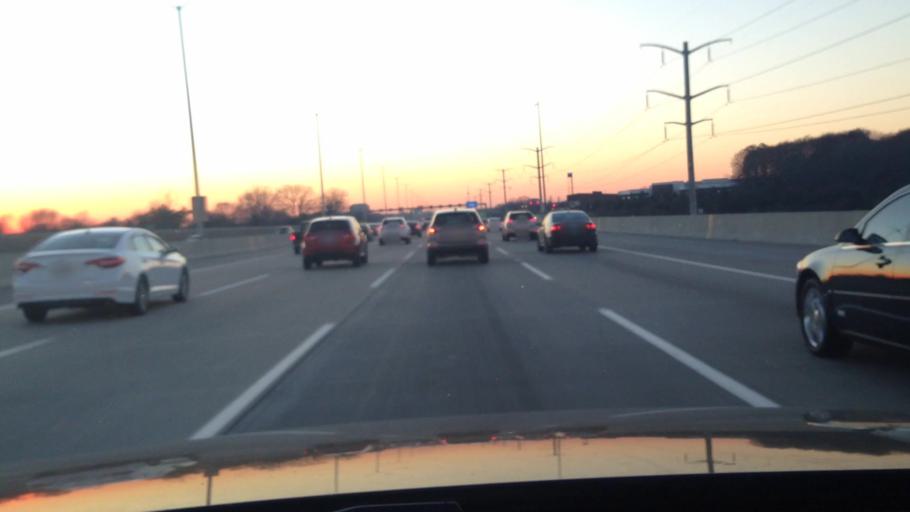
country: US
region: Illinois
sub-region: Cook County
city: South Barrington
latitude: 42.0670
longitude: -88.1151
